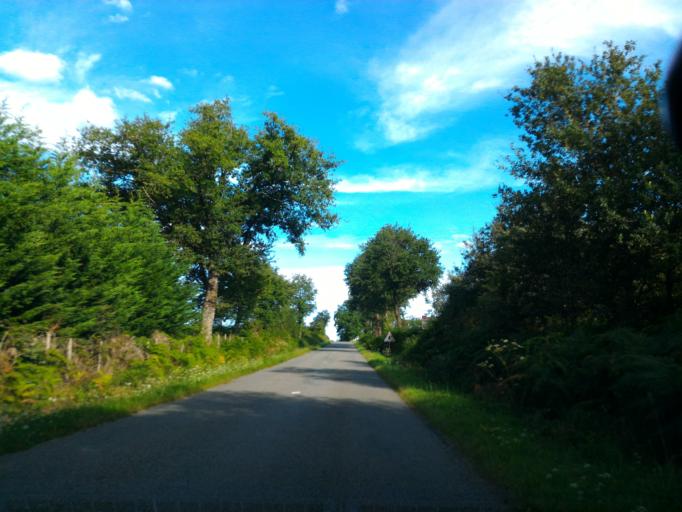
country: FR
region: Poitou-Charentes
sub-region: Departement de la Charente
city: Brigueuil
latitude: 45.9901
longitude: 0.8849
